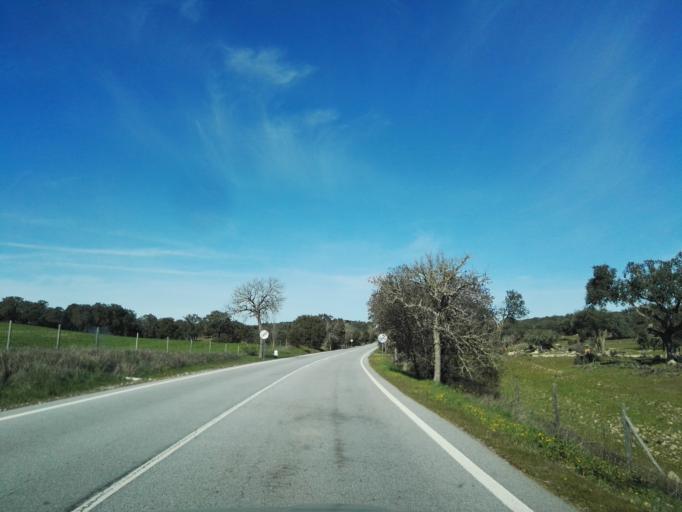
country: PT
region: Portalegre
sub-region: Arronches
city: Arronches
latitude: 39.0683
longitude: -7.2768
